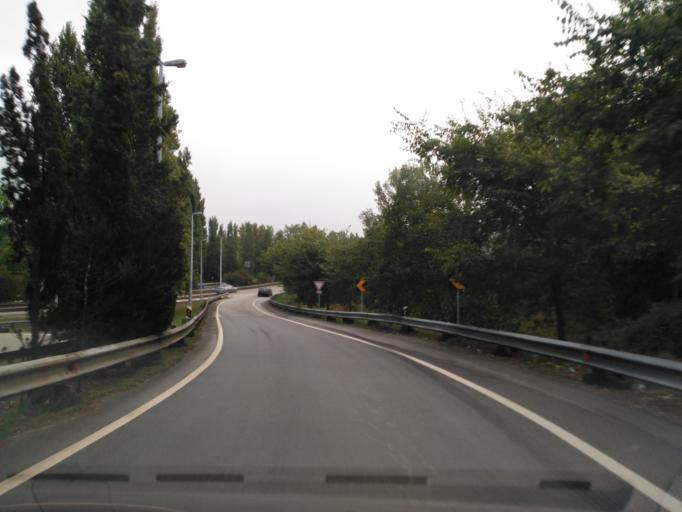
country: PT
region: Braga
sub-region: Guimaraes
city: Guimaraes
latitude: 41.4398
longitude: -8.3075
